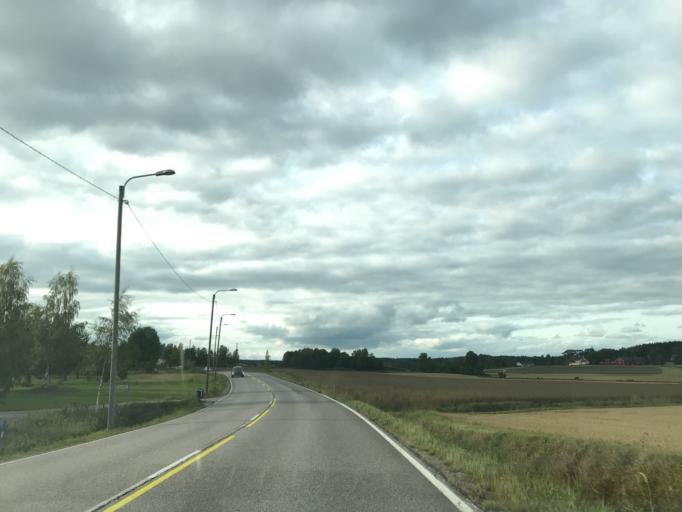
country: FI
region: Uusimaa
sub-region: Helsinki
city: Kirkkonummi
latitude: 60.2430
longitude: 24.4517
